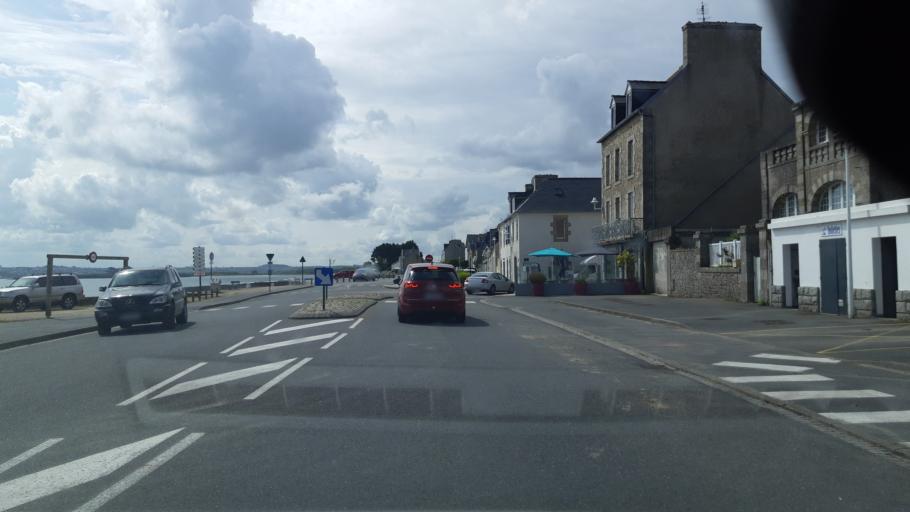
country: FR
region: Brittany
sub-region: Departement du Finistere
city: Saint-Pol-de-Leon
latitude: 48.6831
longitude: -3.9711
